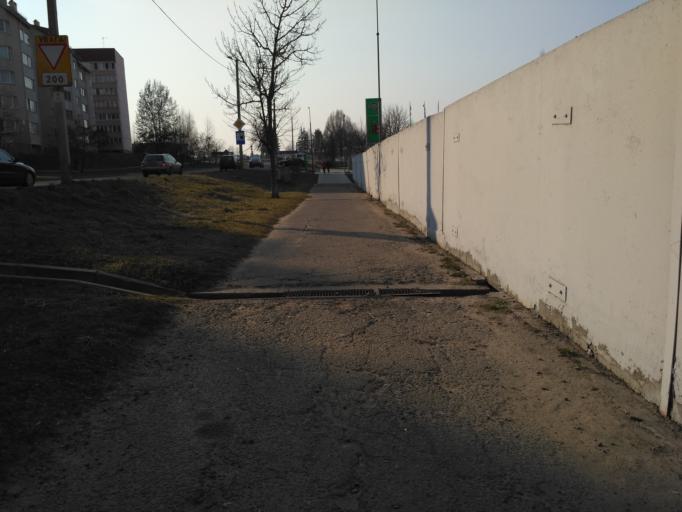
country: BY
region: Minsk
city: Zaslawye
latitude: 54.0137
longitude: 27.2605
